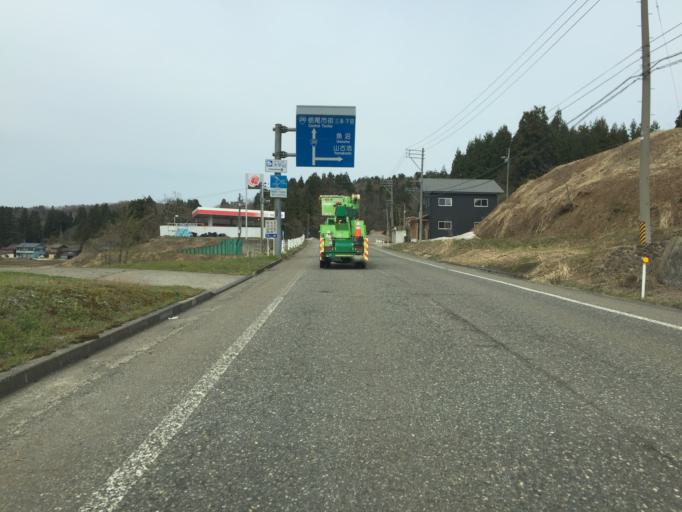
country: JP
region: Niigata
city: Tochio-honcho
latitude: 37.4569
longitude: 138.9702
